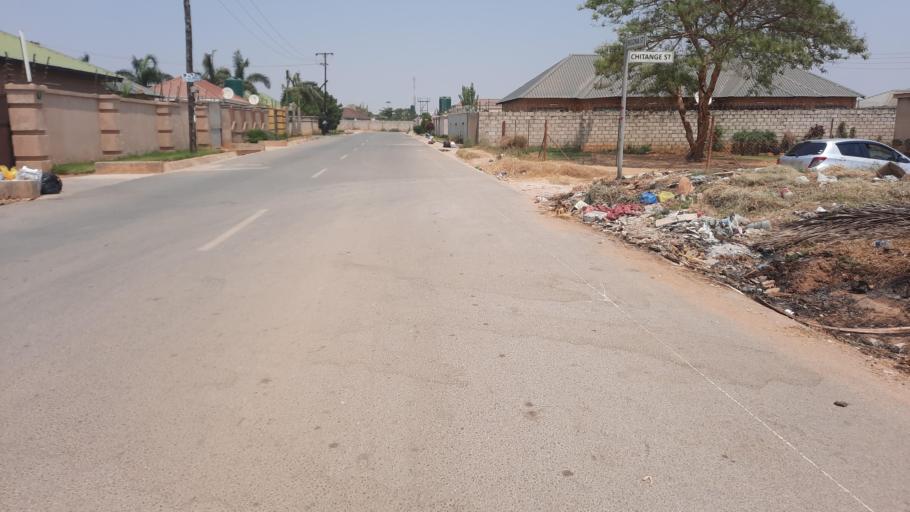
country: ZM
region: Lusaka
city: Lusaka
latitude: -15.3955
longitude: 28.3860
